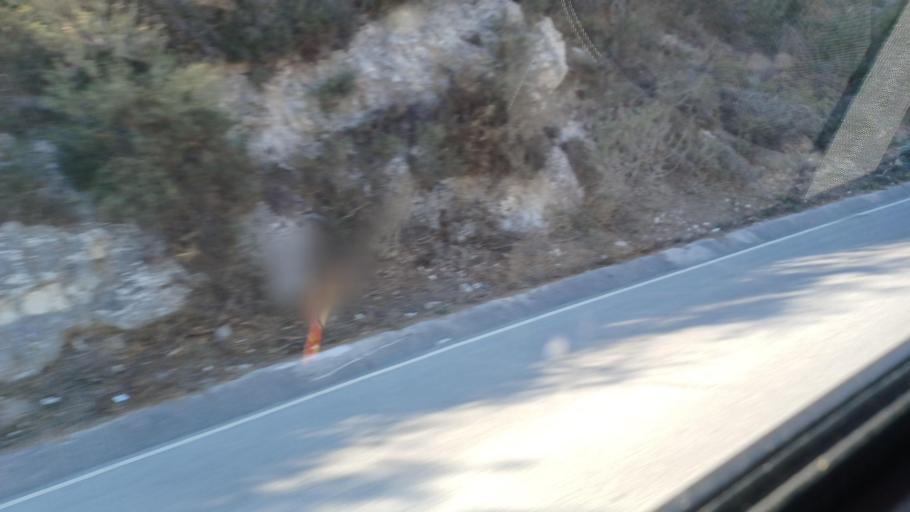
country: CY
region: Pafos
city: Tala
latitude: 34.8428
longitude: 32.4425
